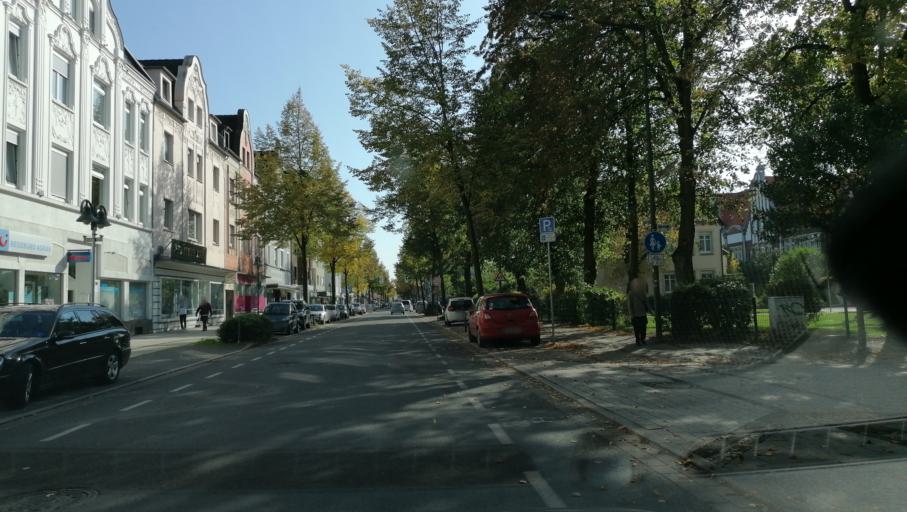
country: DE
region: North Rhine-Westphalia
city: Waltrop
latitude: 51.5997
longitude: 7.4373
